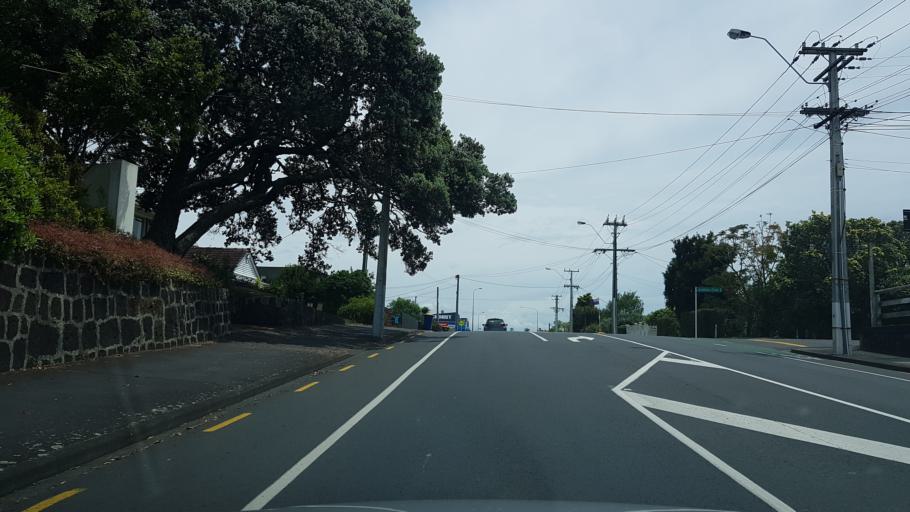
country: NZ
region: Auckland
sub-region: Auckland
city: North Shore
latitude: -36.8146
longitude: 174.7931
